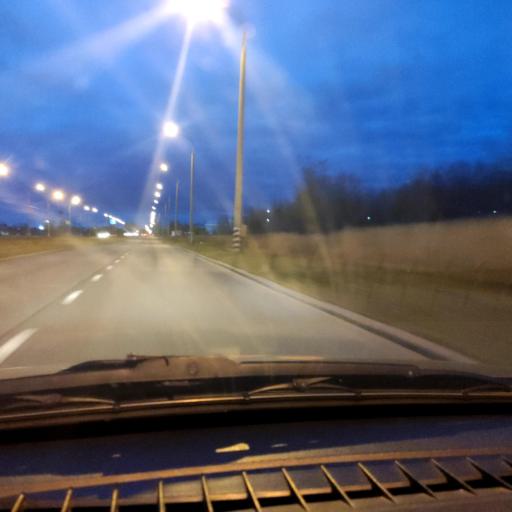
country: RU
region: Samara
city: Tol'yatti
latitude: 53.5571
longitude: 49.3369
